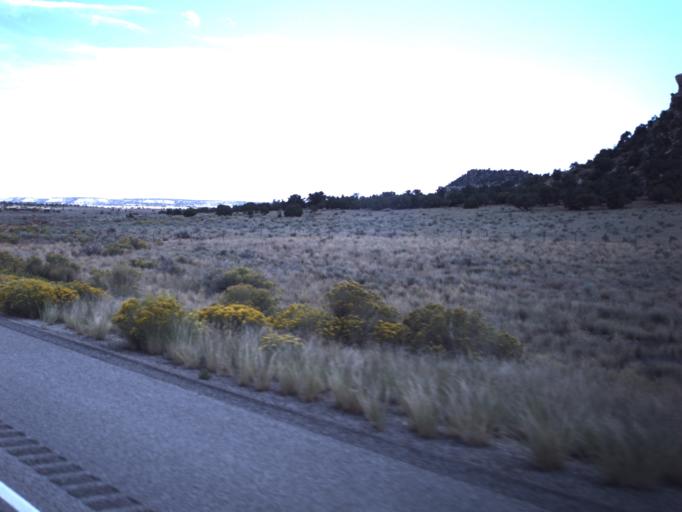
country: US
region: Utah
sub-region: Emery County
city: Castle Dale
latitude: 38.8741
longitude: -110.7401
